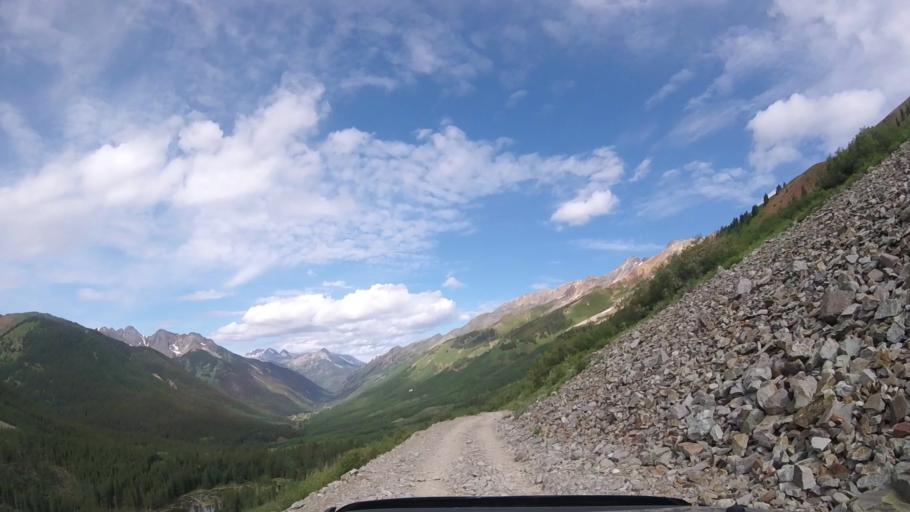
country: US
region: Colorado
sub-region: San Miguel County
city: Telluride
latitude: 37.8574
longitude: -107.7893
